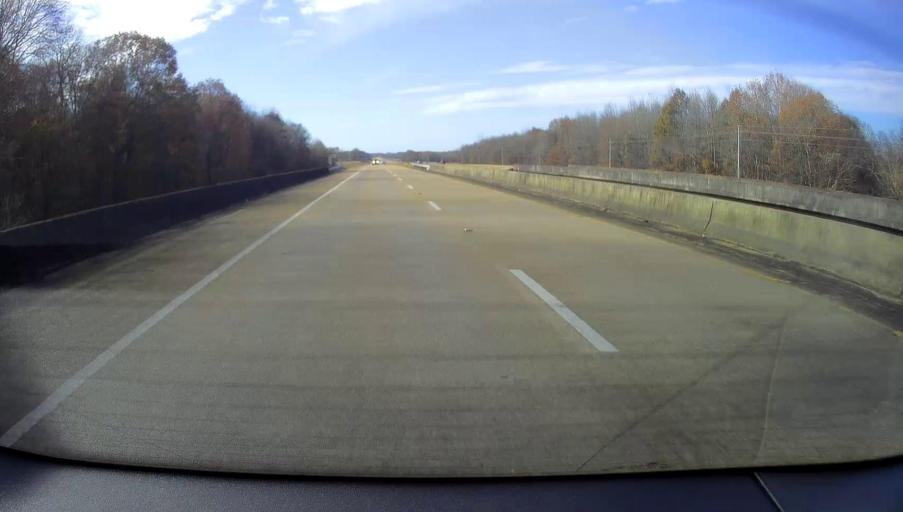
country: US
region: Mississippi
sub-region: Alcorn County
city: Corinth
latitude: 34.9310
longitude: -88.5968
